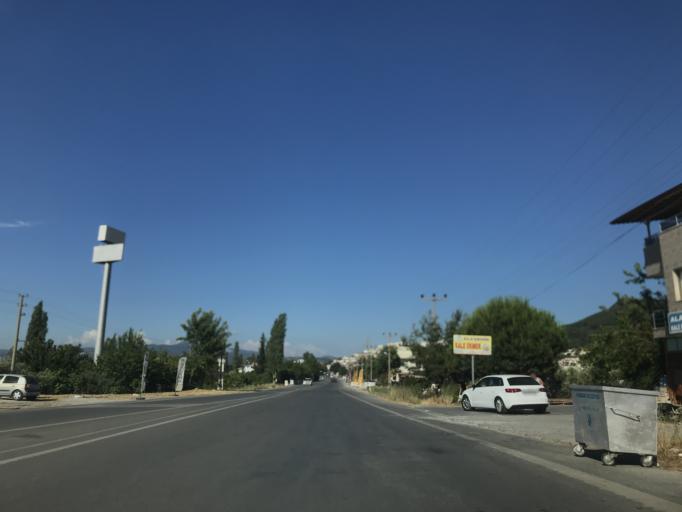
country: TR
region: Aydin
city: Davutlar
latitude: 37.7184
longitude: 27.2432
